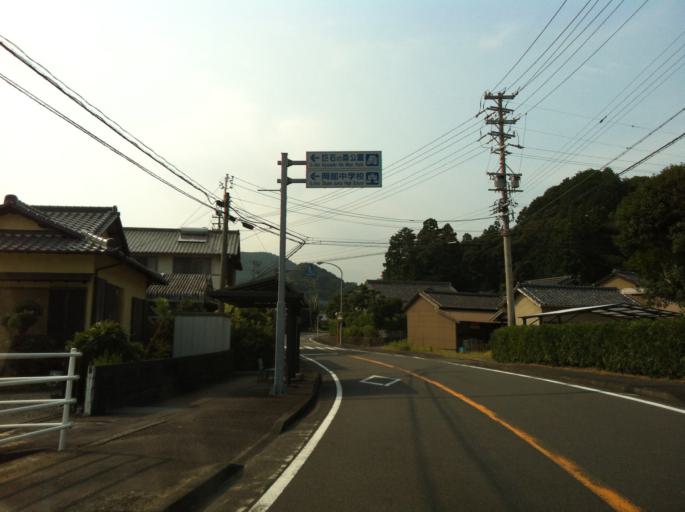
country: JP
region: Shizuoka
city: Fujieda
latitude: 34.9129
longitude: 138.2701
